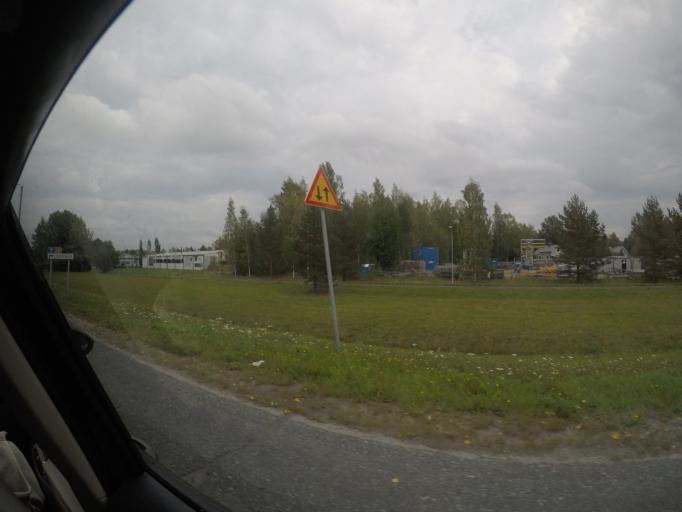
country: FI
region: Haeme
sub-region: Haemeenlinna
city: Haemeenlinna
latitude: 61.0170
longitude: 24.4203
